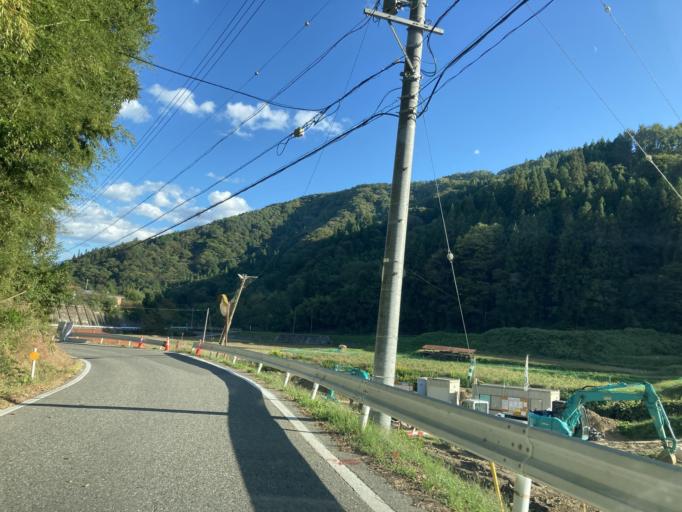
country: JP
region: Nagano
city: Omachi
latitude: 36.4720
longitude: 137.9365
